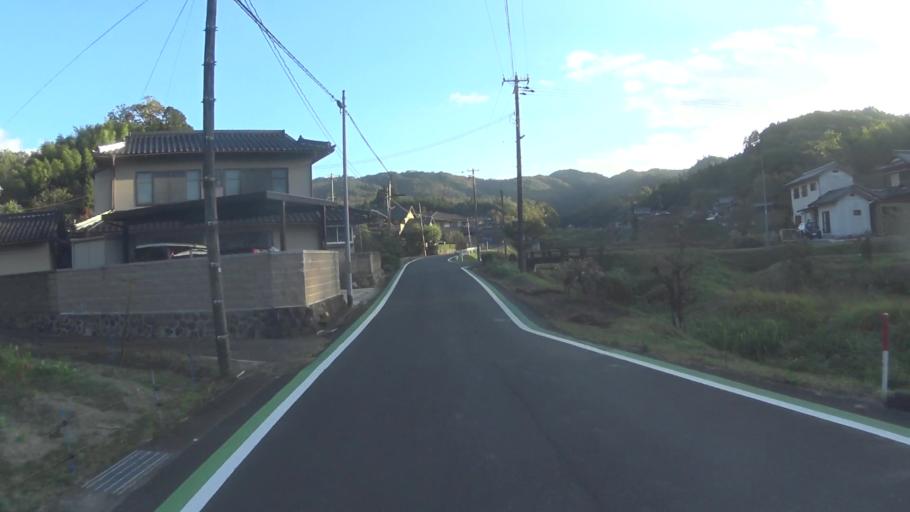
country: JP
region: Kyoto
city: Ayabe
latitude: 35.2832
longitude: 135.2503
